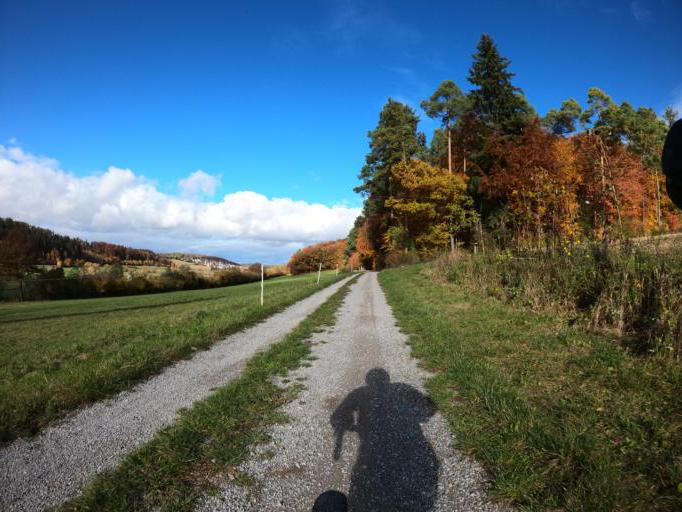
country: DE
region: Baden-Wuerttemberg
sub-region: Regierungsbezirk Stuttgart
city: Aidlingen
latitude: 48.7024
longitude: 8.9010
